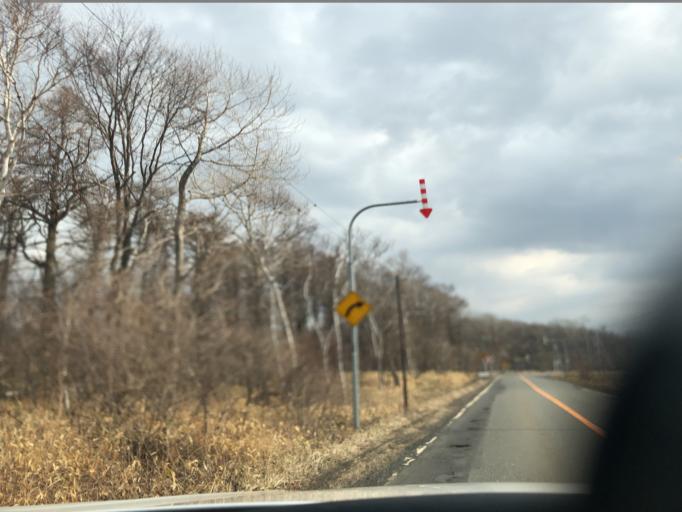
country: JP
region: Hokkaido
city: Chitose
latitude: 42.7632
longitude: 141.7280
